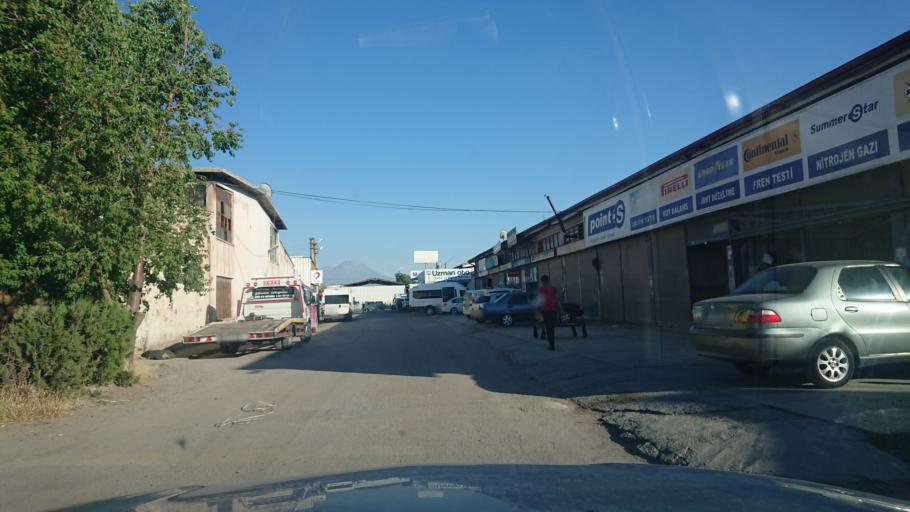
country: TR
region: Aksaray
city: Aksaray
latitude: 38.3735
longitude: 33.9932
